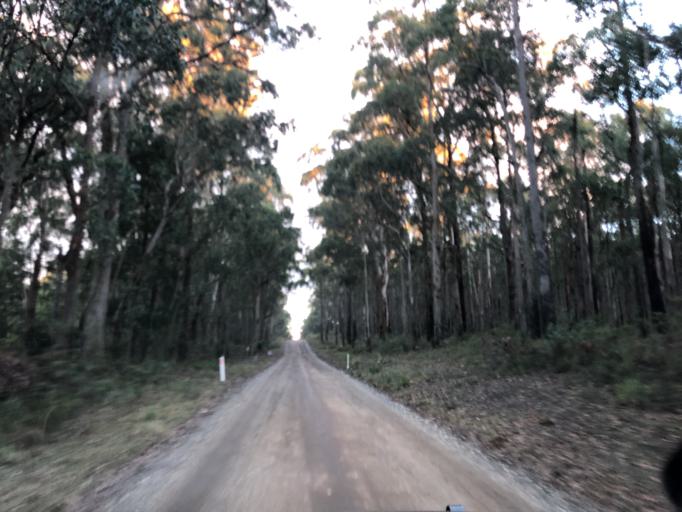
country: AU
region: Victoria
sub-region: Moorabool
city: Bacchus Marsh
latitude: -37.4207
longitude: 144.3984
